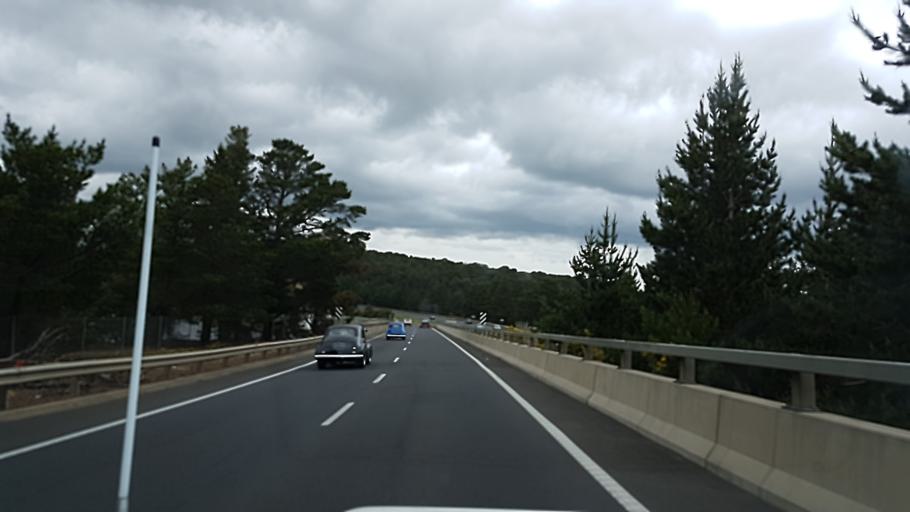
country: AU
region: Victoria
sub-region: Moorabool
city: Bacchus Marsh
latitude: -37.6099
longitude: 144.2941
